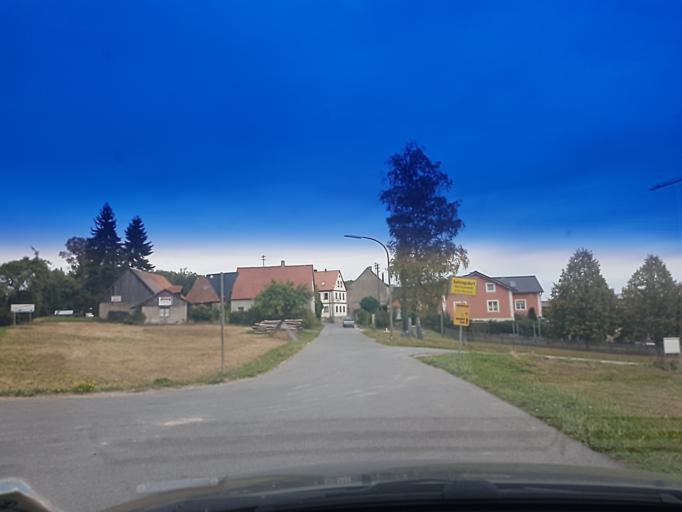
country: DE
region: Bavaria
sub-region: Upper Franconia
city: Burgwindheim
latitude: 49.8653
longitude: 10.5876
